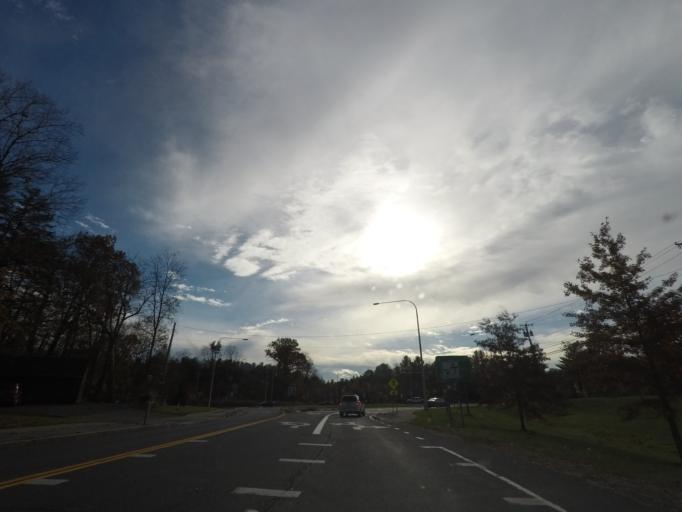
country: US
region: New York
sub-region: Albany County
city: Delmar
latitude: 42.6378
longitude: -73.8555
